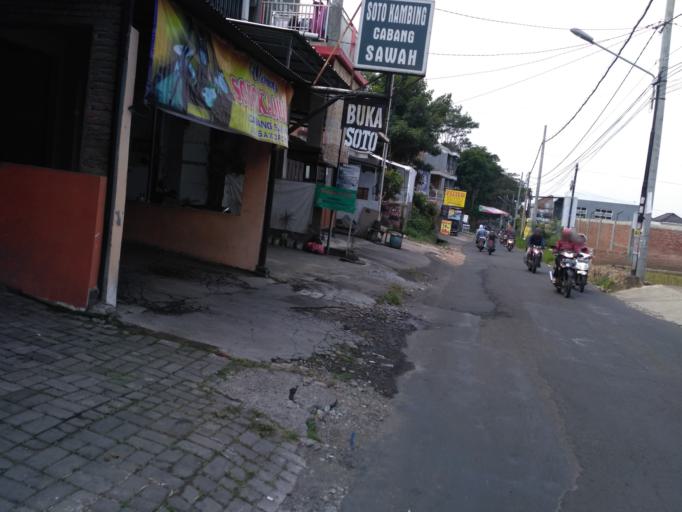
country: ID
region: East Java
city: Malang
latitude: -7.9245
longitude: 112.6038
